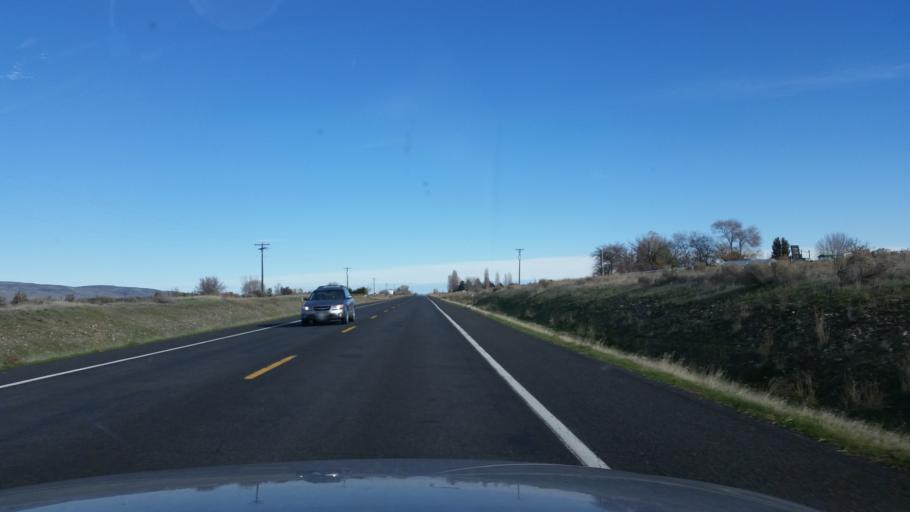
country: US
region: Washington
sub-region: Grant County
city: Ephrata
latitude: 47.2048
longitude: -119.6693
